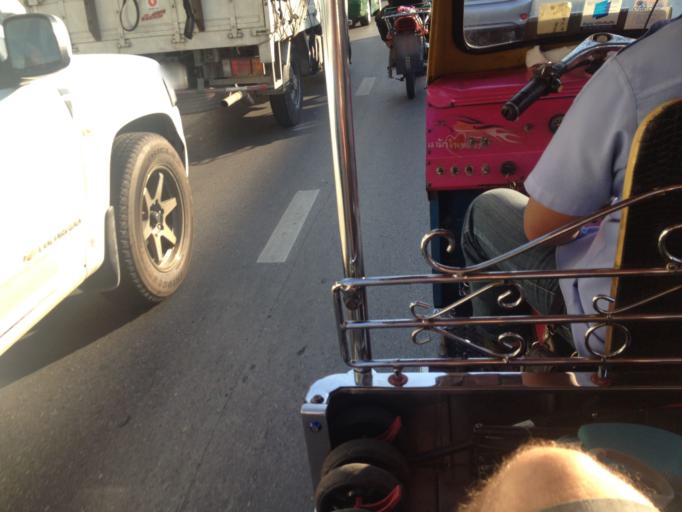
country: TH
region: Bangkok
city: Bangkok
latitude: 13.7546
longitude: 100.5052
